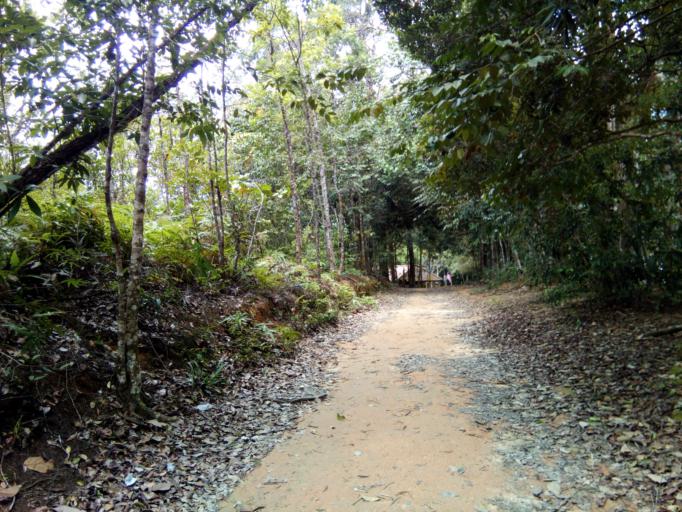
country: MY
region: Penang
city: Tanjung Tokong
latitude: 5.4370
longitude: 100.2822
